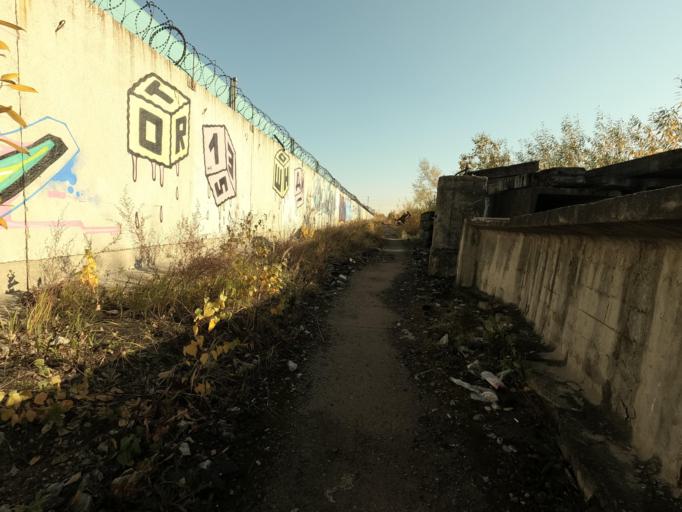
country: RU
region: St.-Petersburg
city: Obukhovo
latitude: 59.8456
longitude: 30.4633
